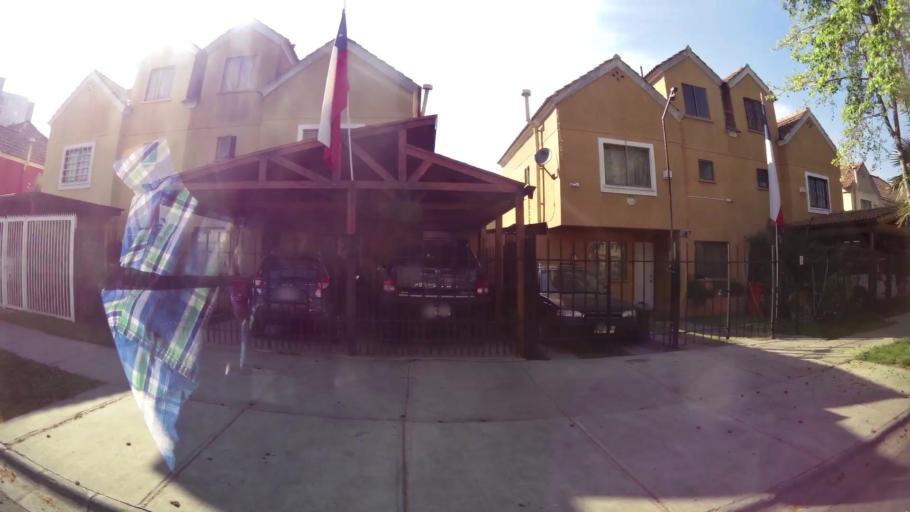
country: CL
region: Santiago Metropolitan
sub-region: Provincia de Santiago
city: Lo Prado
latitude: -33.4515
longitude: -70.7603
